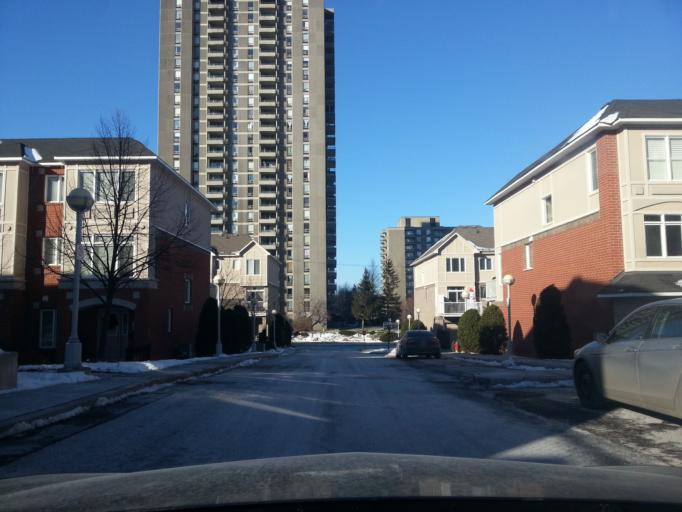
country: CA
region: Ontario
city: Ottawa
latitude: 45.3984
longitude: -75.7506
